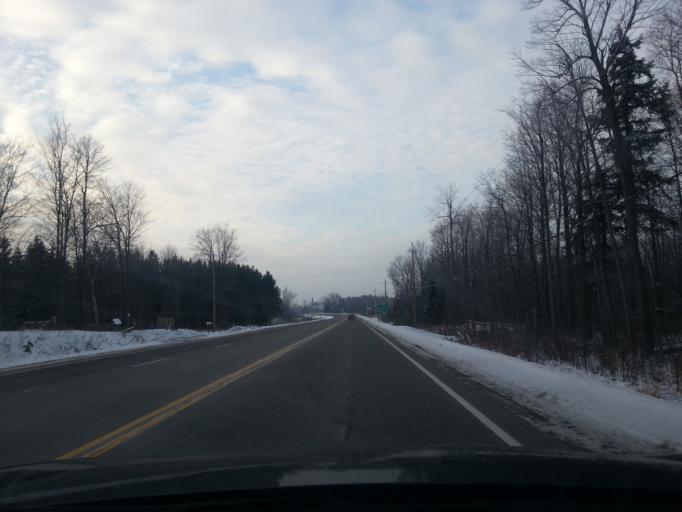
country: CA
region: Ontario
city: Carleton Place
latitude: 45.0912
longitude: -76.2421
